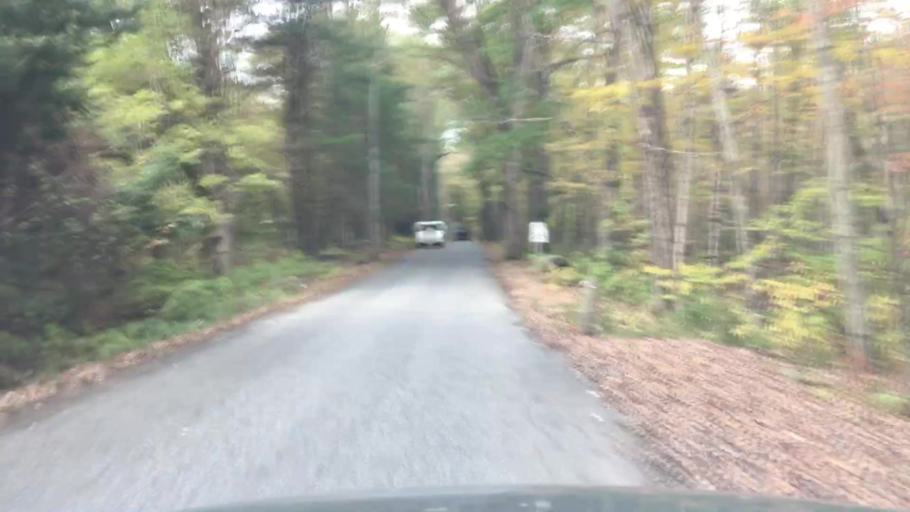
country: US
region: Connecticut
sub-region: Tolland County
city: Storrs
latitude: 41.8776
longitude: -72.1695
